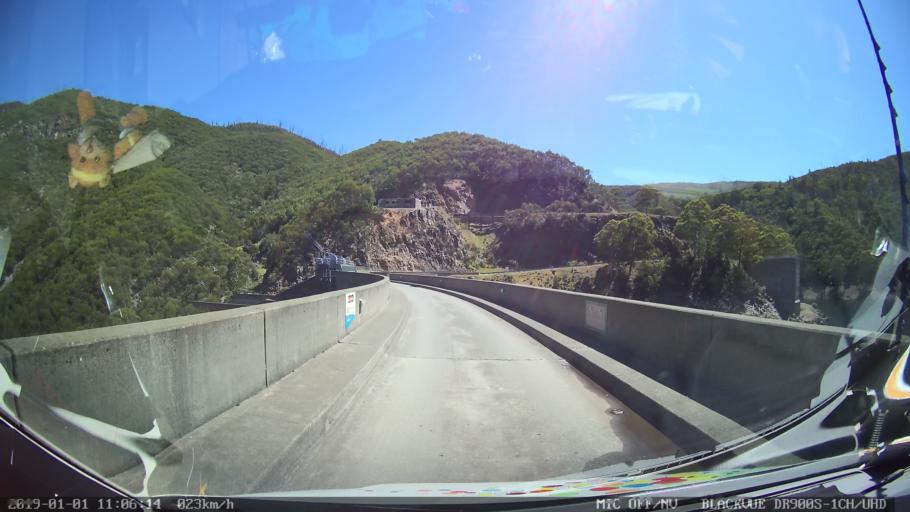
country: AU
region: New South Wales
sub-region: Snowy River
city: Jindabyne
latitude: -35.9649
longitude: 148.3899
